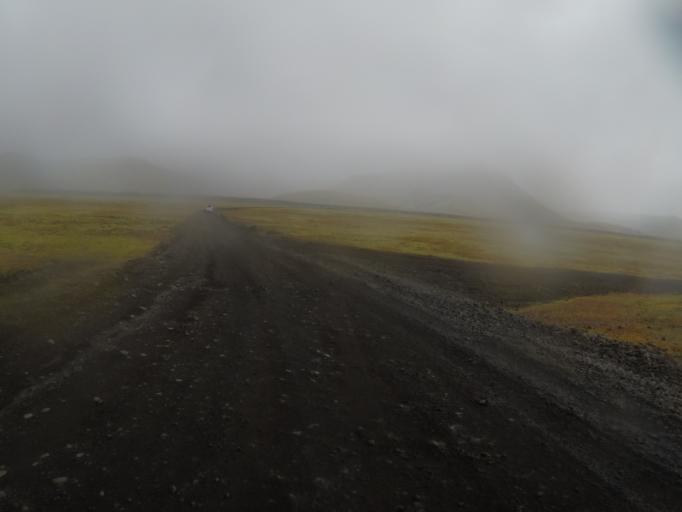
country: IS
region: South
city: Vestmannaeyjar
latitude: 63.9704
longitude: -18.8085
